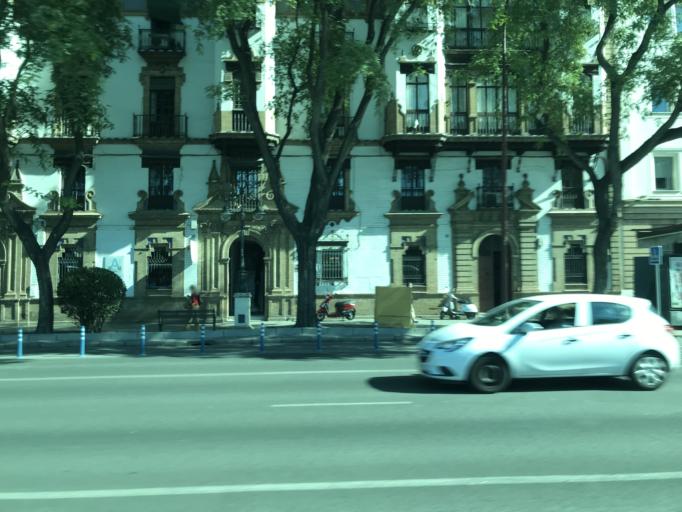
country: ES
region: Andalusia
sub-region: Provincia de Sevilla
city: Sevilla
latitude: 37.3844
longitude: -5.9980
